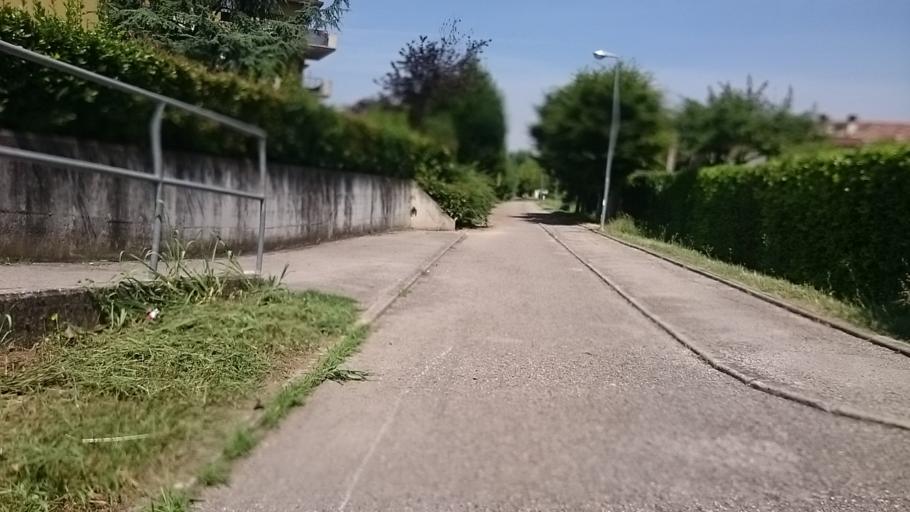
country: IT
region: Veneto
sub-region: Provincia di Vicenza
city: Longare
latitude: 45.4755
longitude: 11.6096
